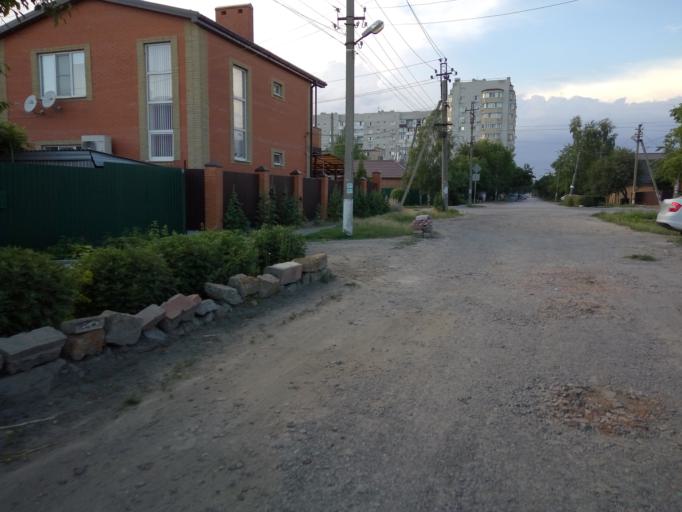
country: RU
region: Rostov
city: Bataysk
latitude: 47.1203
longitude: 39.7356
